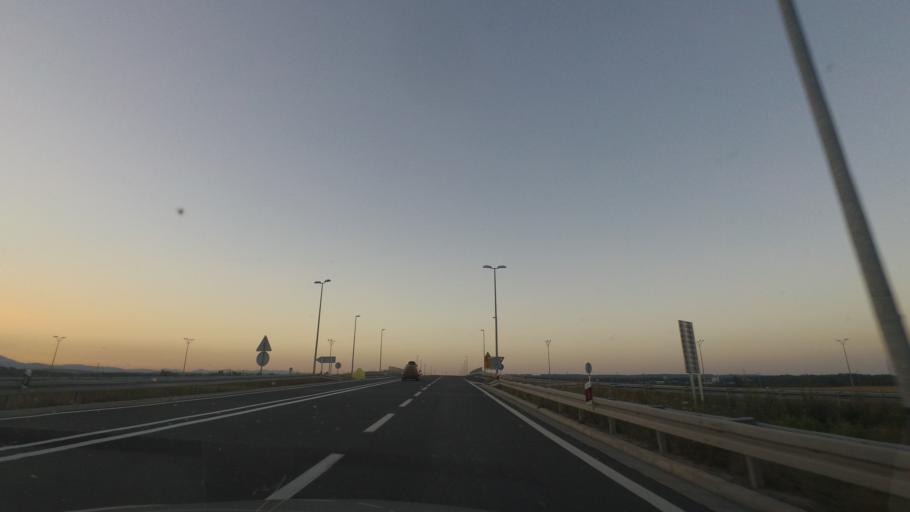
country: HR
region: Grad Zagreb
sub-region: Sesvete
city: Sesvete
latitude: 45.7910
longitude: 16.1639
